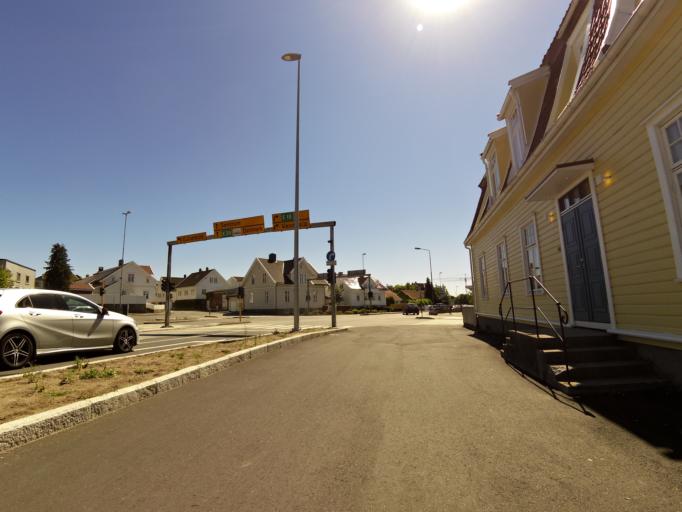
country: NO
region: Vest-Agder
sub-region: Kristiansand
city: Kristiansand
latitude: 58.1520
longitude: 8.0084
